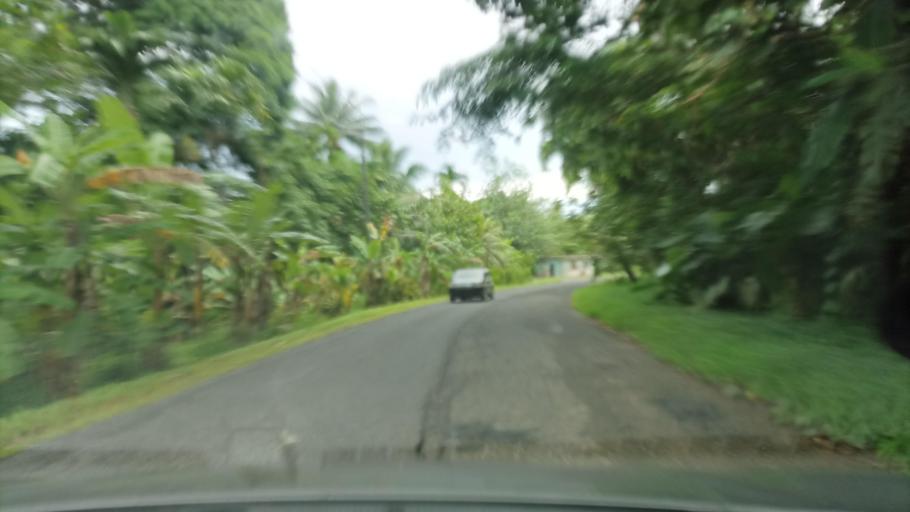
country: FM
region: Pohnpei
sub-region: Kolonia Municipality
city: Kolonia
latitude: 6.9515
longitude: 158.2362
